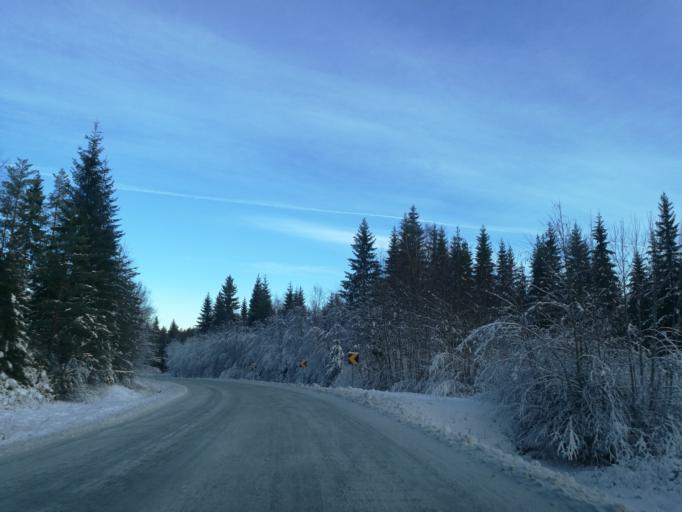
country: NO
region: Hedmark
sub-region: Grue
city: Kirkenaer
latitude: 60.3087
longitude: 12.2613
